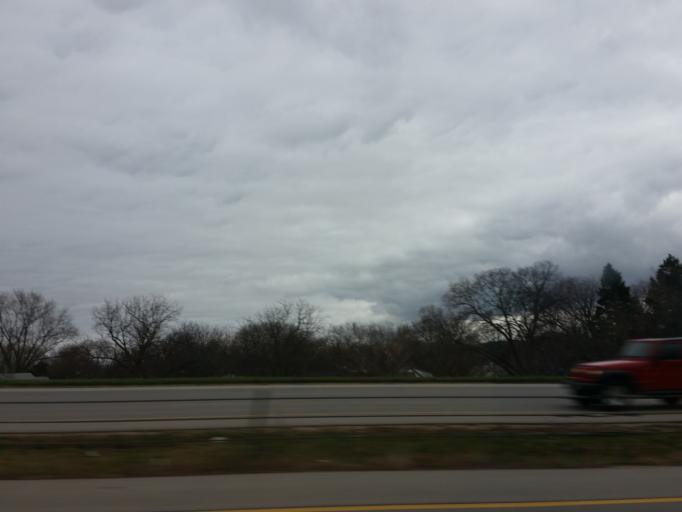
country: US
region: Iowa
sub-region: Linn County
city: Cedar Rapids
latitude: 41.9658
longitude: -91.6709
